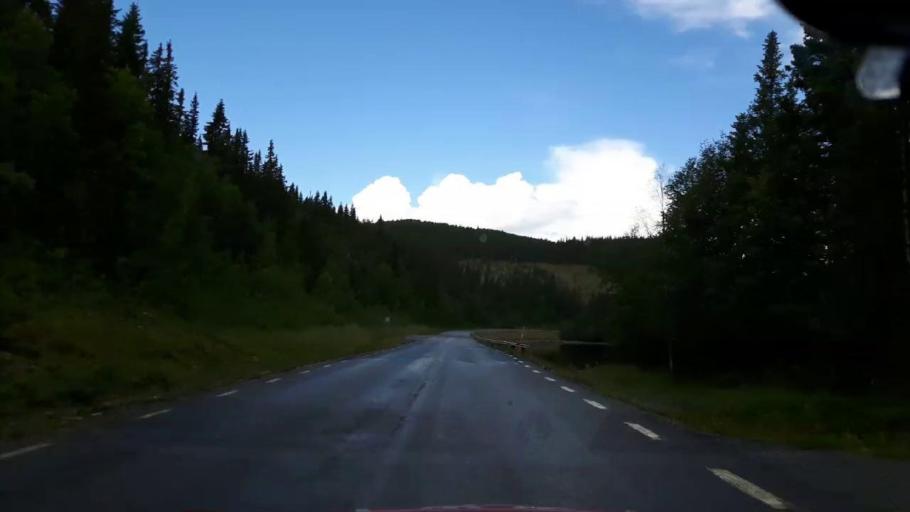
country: SE
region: Vaesterbotten
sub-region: Vilhelmina Kommun
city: Sjoberg
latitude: 64.9958
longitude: 15.2115
